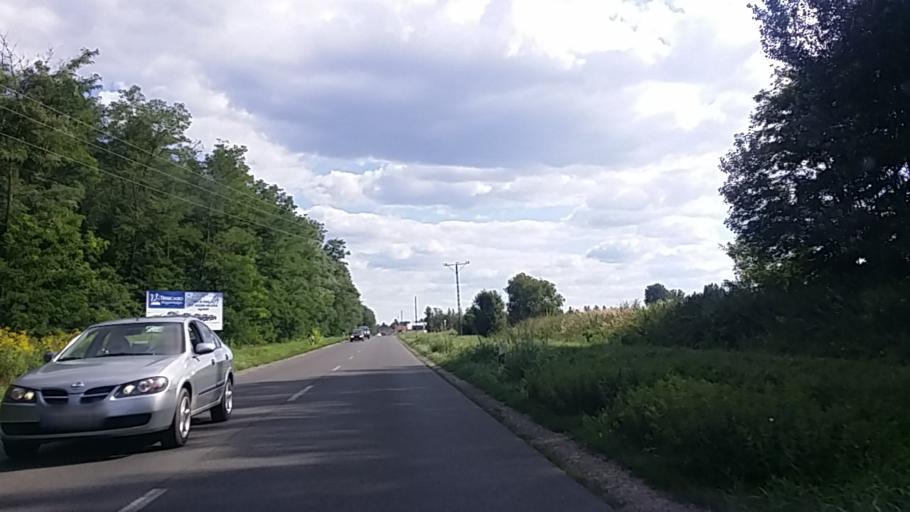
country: HU
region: Tolna
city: Dombovar
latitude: 46.3408
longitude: 18.1269
